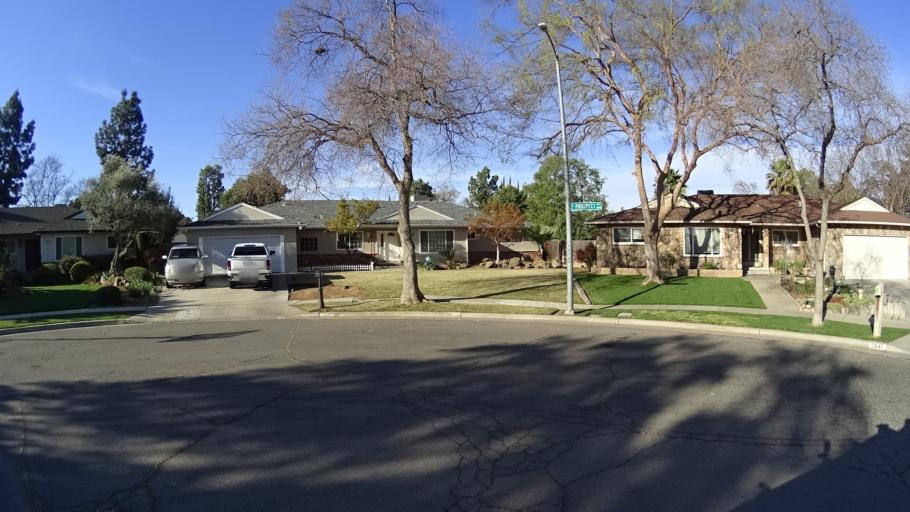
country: US
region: California
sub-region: Fresno County
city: Fresno
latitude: 36.8200
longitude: -119.8506
